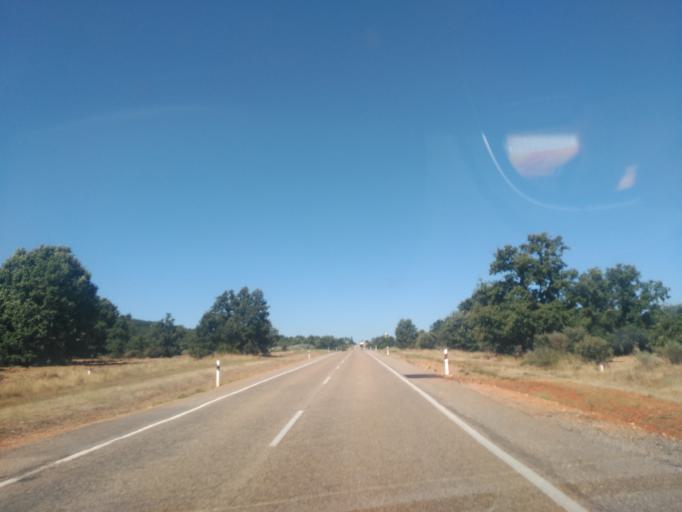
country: ES
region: Castille and Leon
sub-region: Provincia de Zamora
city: Otero de Bodas
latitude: 41.9355
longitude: -6.1332
